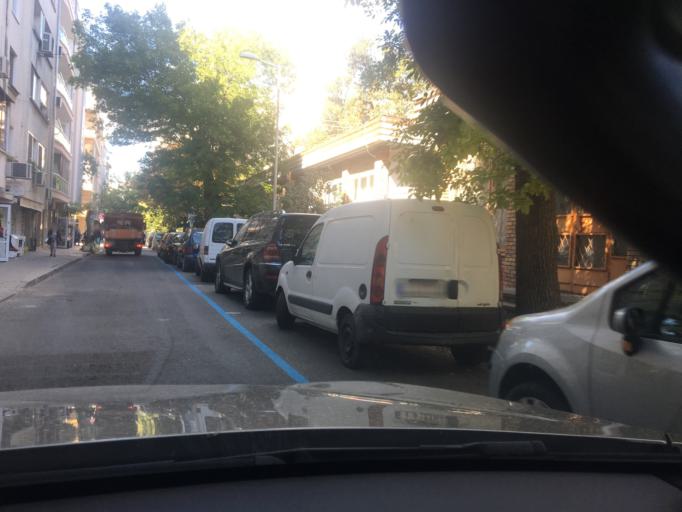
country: BG
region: Burgas
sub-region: Obshtina Burgas
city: Burgas
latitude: 42.4999
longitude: 27.4747
